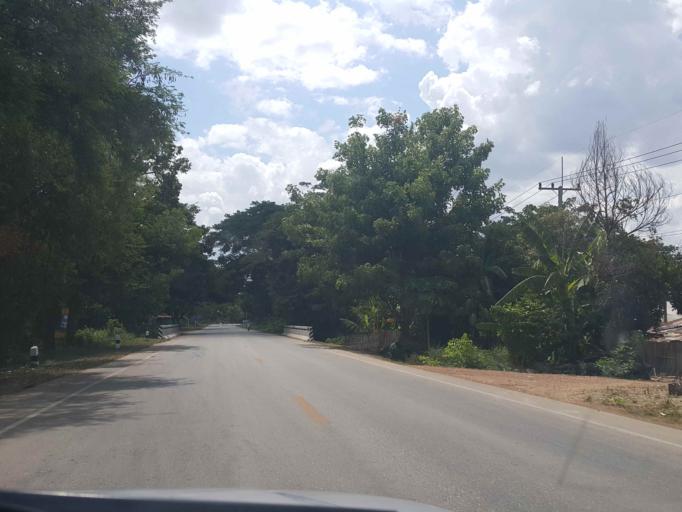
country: TH
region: Sukhothai
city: Thung Saliam
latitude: 17.3294
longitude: 99.6247
